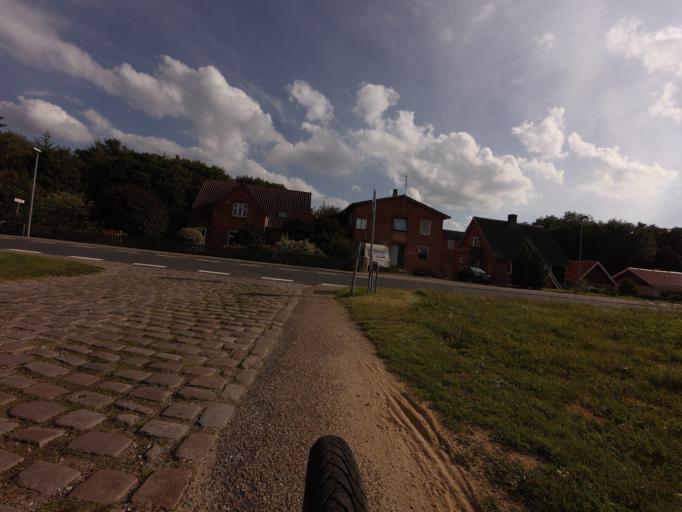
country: DK
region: Central Jutland
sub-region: Viborg Kommune
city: Karup
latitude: 56.3054
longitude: 9.1626
